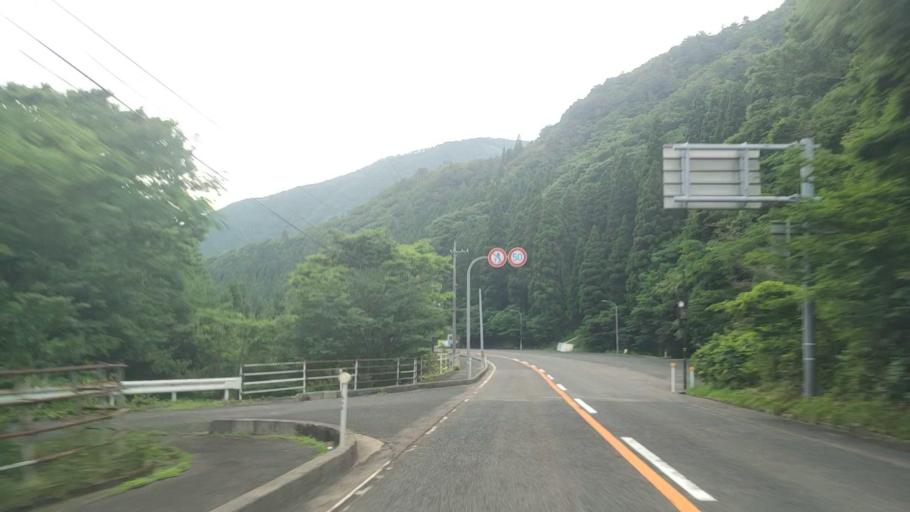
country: JP
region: Tottori
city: Kurayoshi
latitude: 35.3172
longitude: 133.8980
